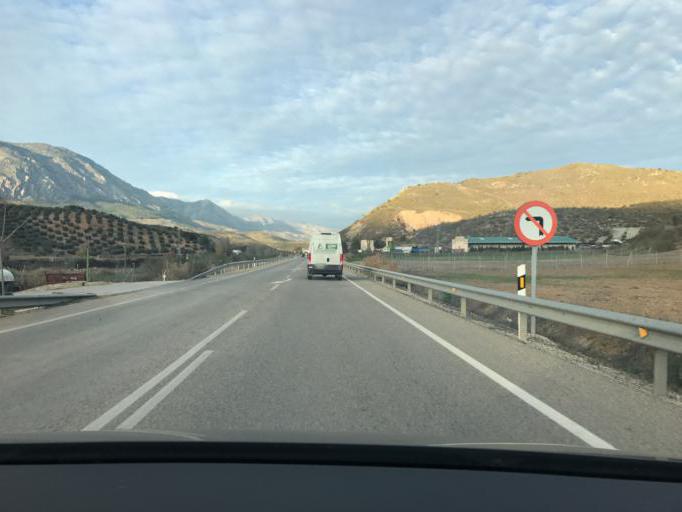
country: ES
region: Andalusia
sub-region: Provincia de Jaen
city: Huelma
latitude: 37.6544
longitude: -3.4204
